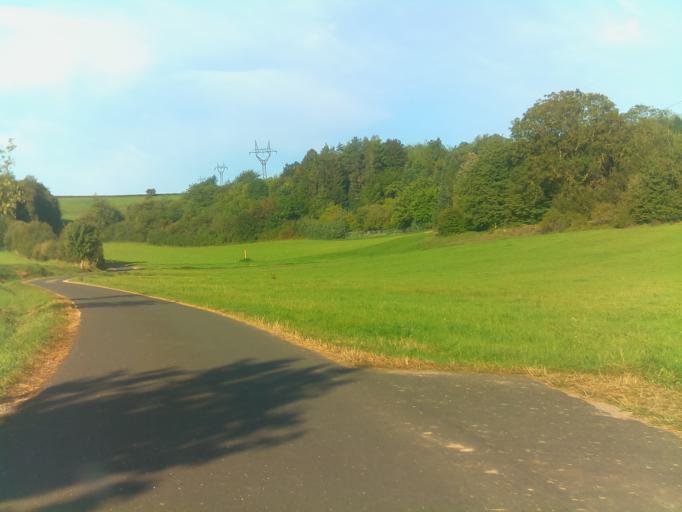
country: DE
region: Thuringia
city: Konigsee
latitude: 50.6557
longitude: 11.0752
